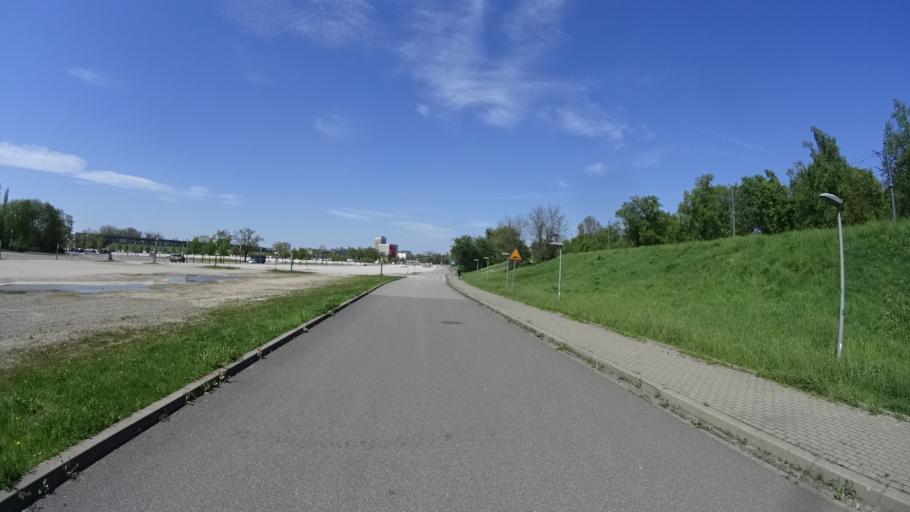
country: PL
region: Masovian Voivodeship
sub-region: Warszawa
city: Praga Polnoc
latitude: 52.2422
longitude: 21.0490
